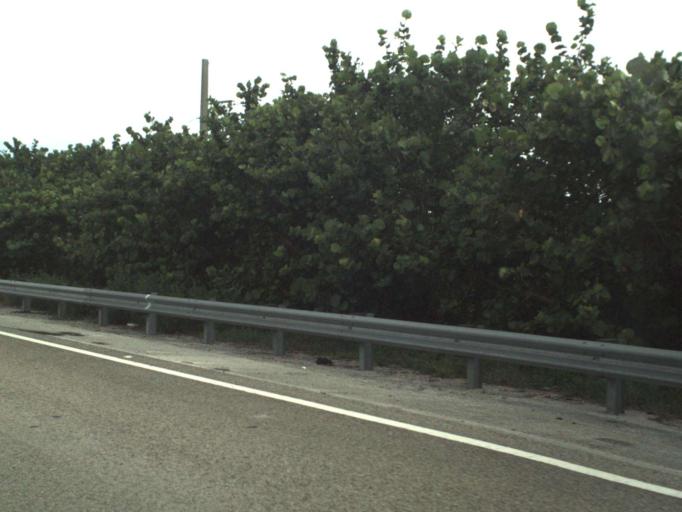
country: US
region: Florida
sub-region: Martin County
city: Palm City
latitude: 27.1154
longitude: -80.2648
